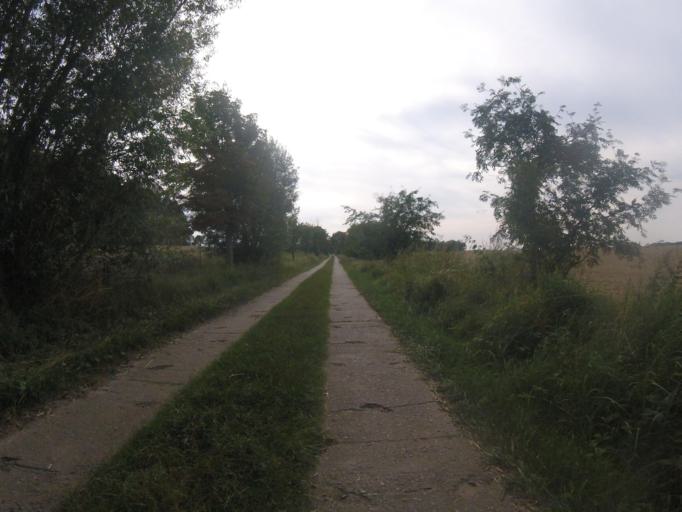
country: DE
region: Brandenburg
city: Mittenwalde
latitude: 52.2792
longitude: 13.4884
